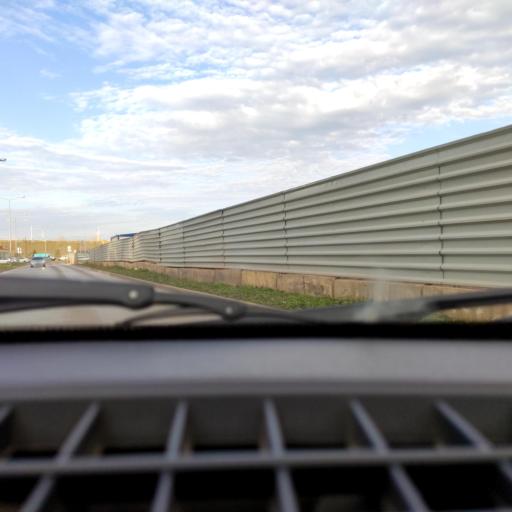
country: RU
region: Bashkortostan
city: Mikhaylovka
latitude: 54.6983
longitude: 55.8587
